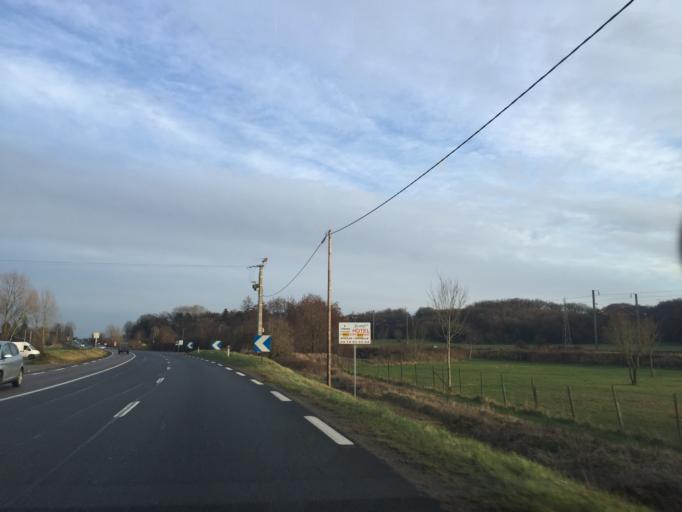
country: FR
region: Rhone-Alpes
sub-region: Departement de l'Isere
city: Vaulx-Milieu
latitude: 45.6122
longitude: 5.2025
